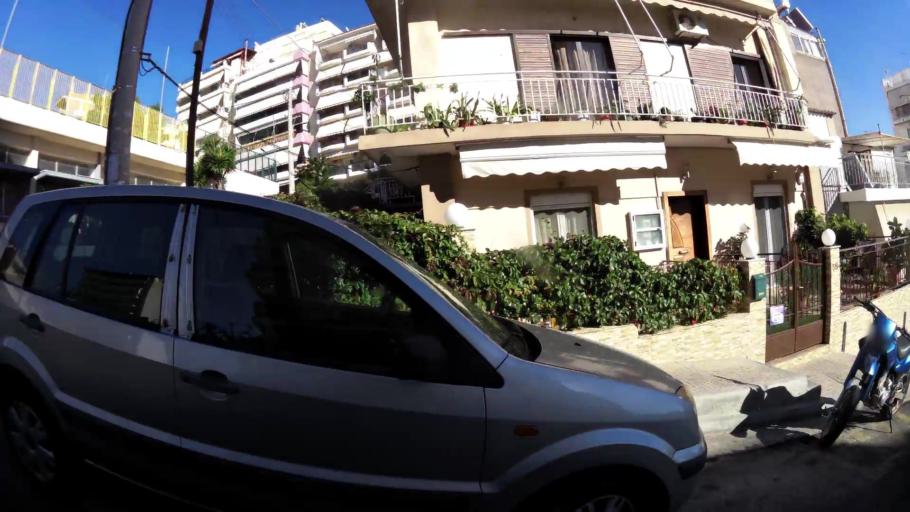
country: GR
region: Attica
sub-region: Nomos Piraios
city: Perama
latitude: 37.9685
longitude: 23.5678
